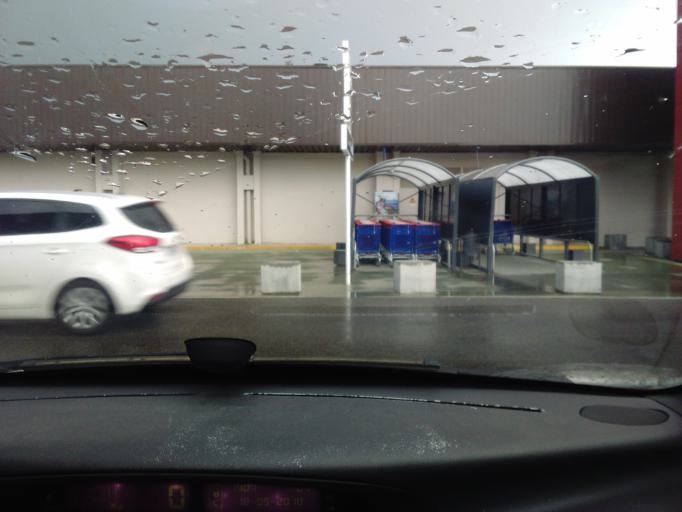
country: ES
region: Andalusia
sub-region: Provincia de Sevilla
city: Sevilla
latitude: 37.4065
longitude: -5.9396
